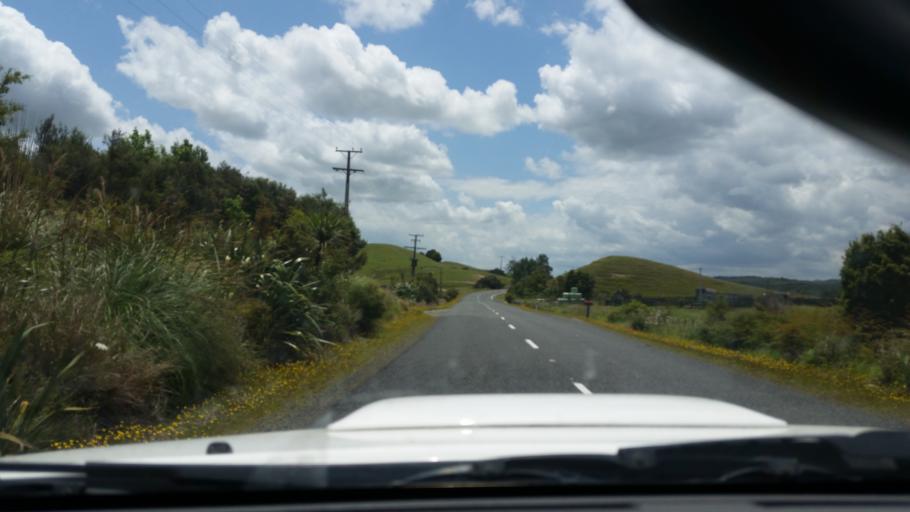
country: NZ
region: Northland
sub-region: Kaipara District
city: Dargaville
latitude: -35.8878
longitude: 173.8413
